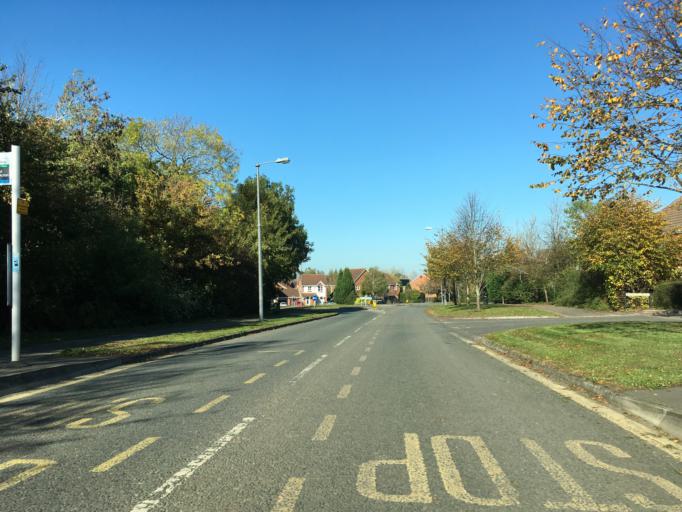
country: GB
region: England
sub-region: South Gloucestershire
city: Yate
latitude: 51.5530
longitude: -2.4111
